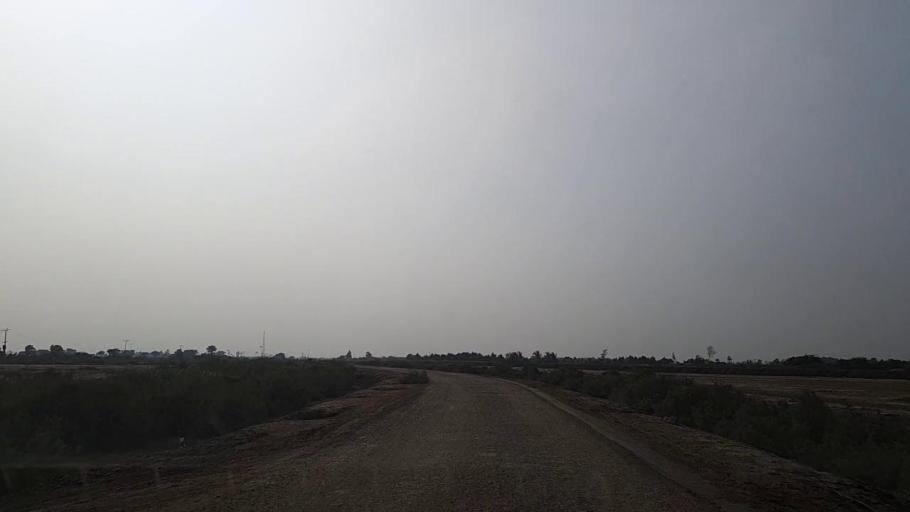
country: PK
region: Sindh
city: Mirpur Sakro
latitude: 24.6430
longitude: 67.6048
